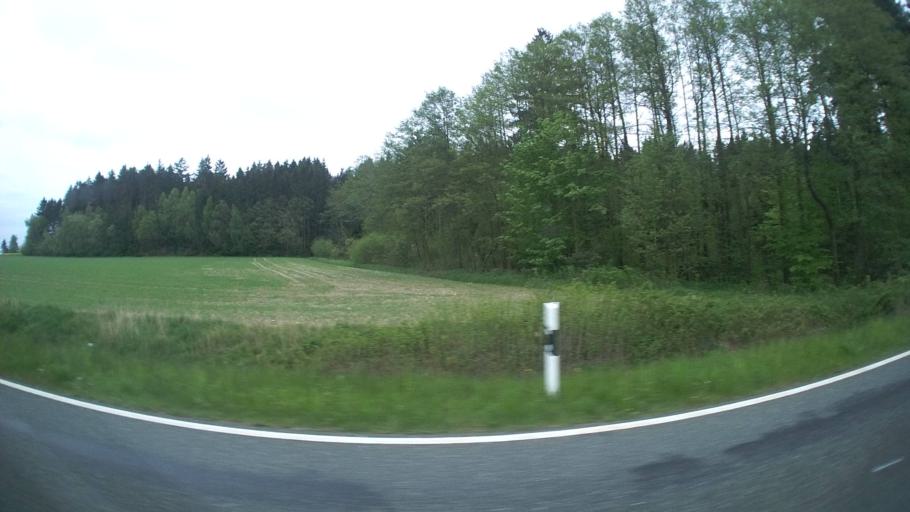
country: DE
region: Bavaria
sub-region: Upper Franconia
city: Zell im Fichtelgebirge
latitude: 50.1419
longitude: 11.8332
